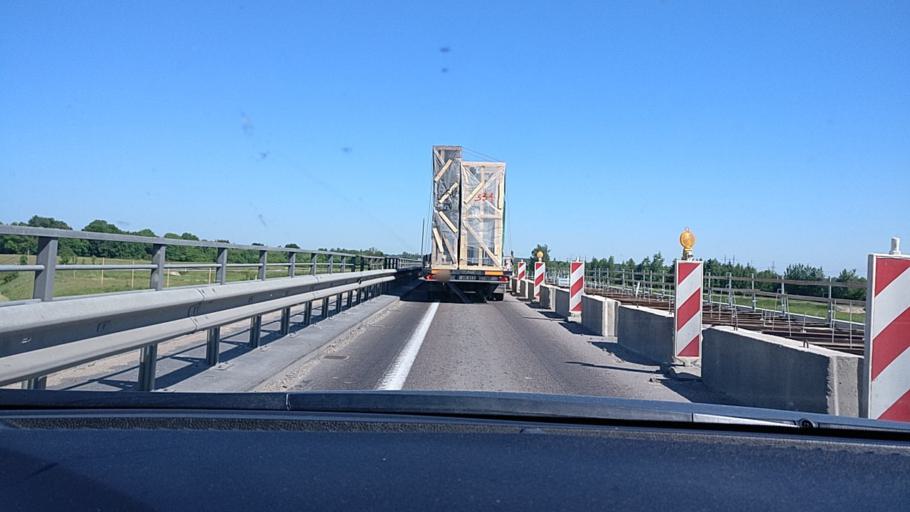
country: LT
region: Panevezys
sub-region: Panevezys City
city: Panevezys
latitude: 55.7336
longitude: 24.2767
